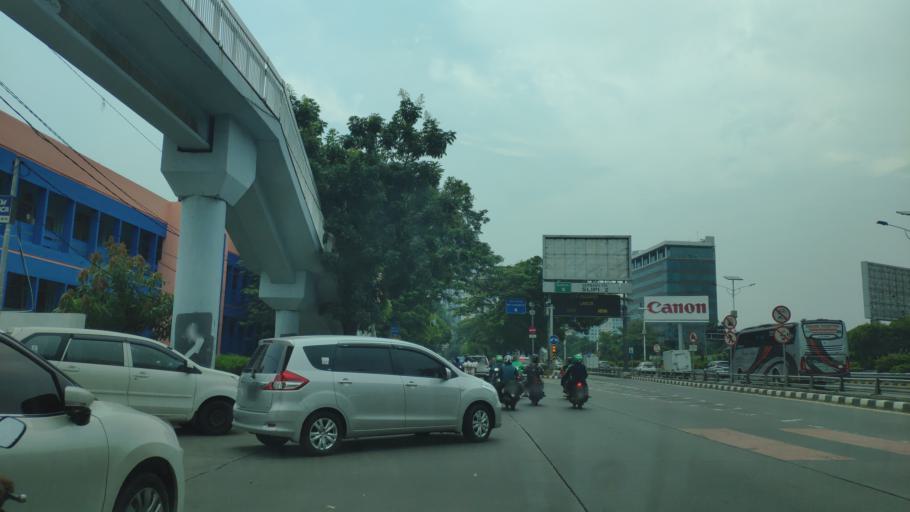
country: ID
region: Jakarta Raya
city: Jakarta
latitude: -6.1937
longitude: 106.7975
